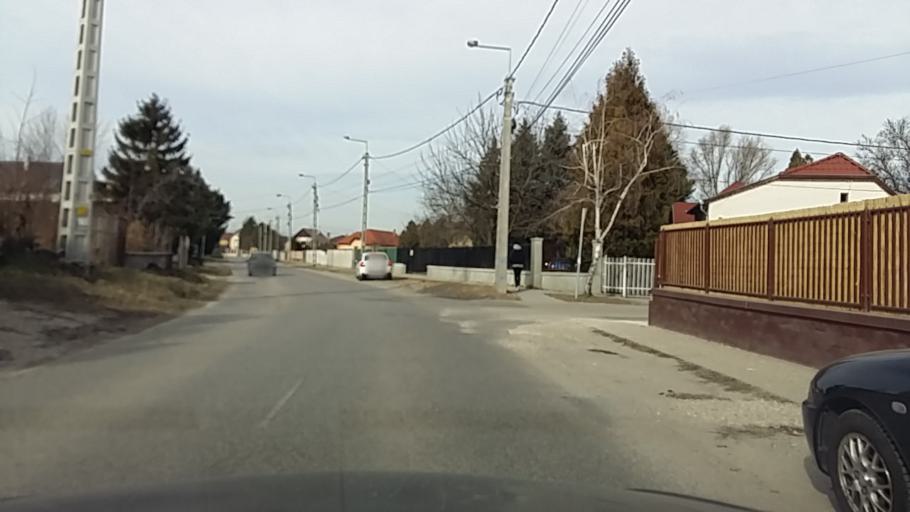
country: HU
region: Pest
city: Szigetszentmiklos
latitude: 47.3447
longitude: 19.0318
